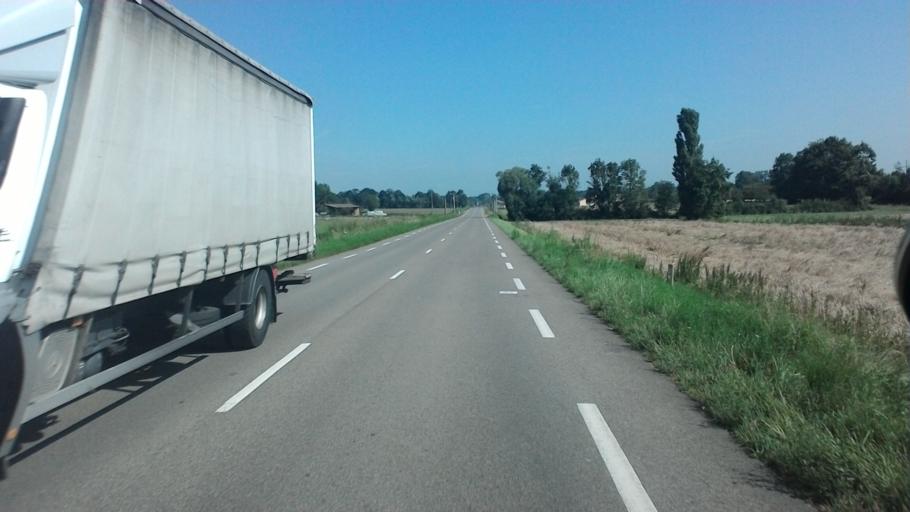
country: FR
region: Rhone-Alpes
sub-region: Departement de l'Ain
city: Montrevel-en-Bresse
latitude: 46.3856
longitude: 5.1167
